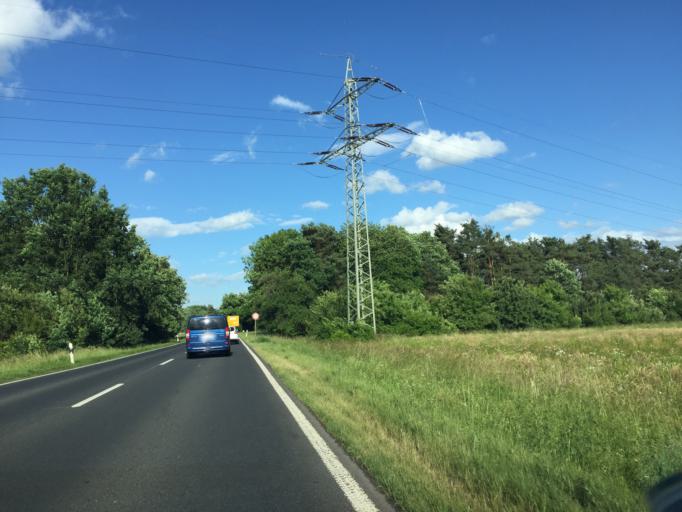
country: DE
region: Bavaria
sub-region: Regierungsbezirk Unterfranken
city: Stockstadt am Main
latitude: 49.9578
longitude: 9.0746
